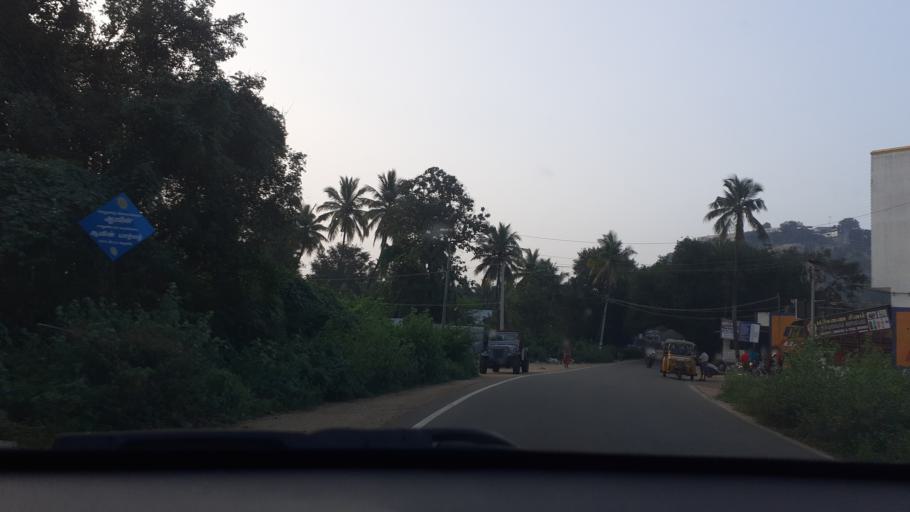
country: IN
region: Tamil Nadu
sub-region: Dindigul
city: Palani
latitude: 10.4307
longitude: 77.5249
